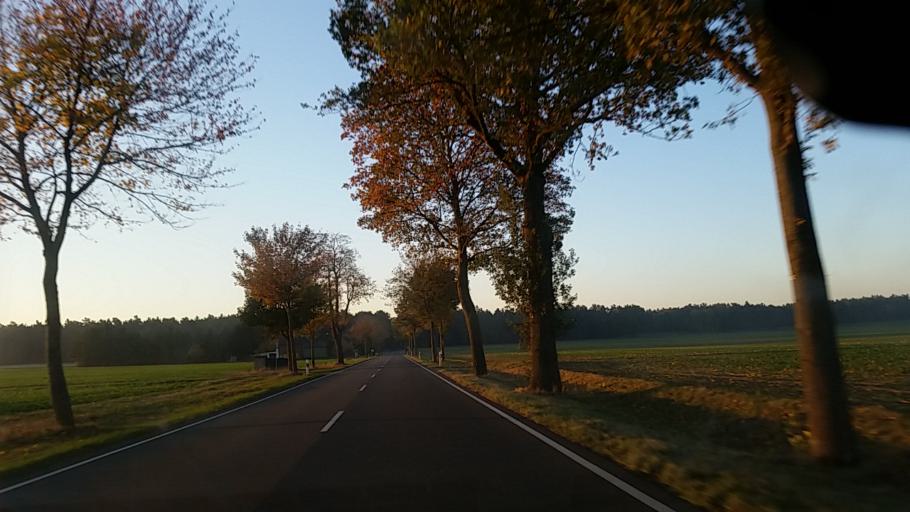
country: DE
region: Lower Saxony
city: Bodenteich
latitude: 52.7905
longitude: 10.7154
